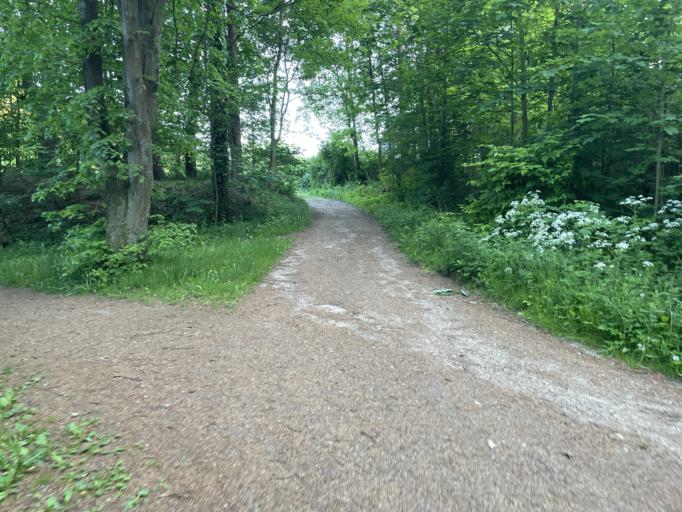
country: DE
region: Schleswig-Holstein
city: Husum
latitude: 54.4731
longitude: 9.0720
